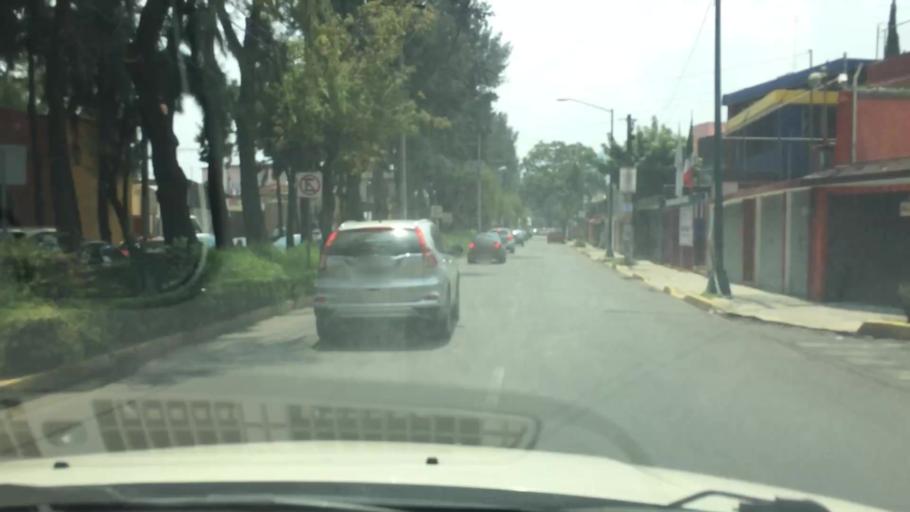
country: MX
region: Mexico City
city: Xochimilco
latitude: 19.2824
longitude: -99.1254
